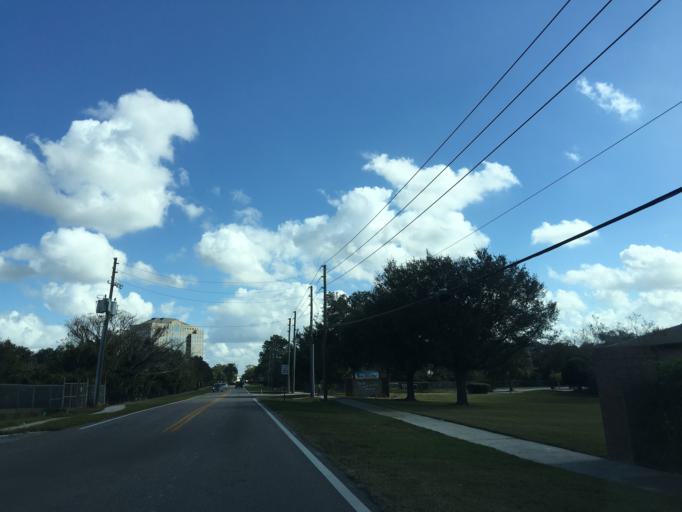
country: US
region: Florida
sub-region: Orange County
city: Eatonville
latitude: 28.6328
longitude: -81.4090
